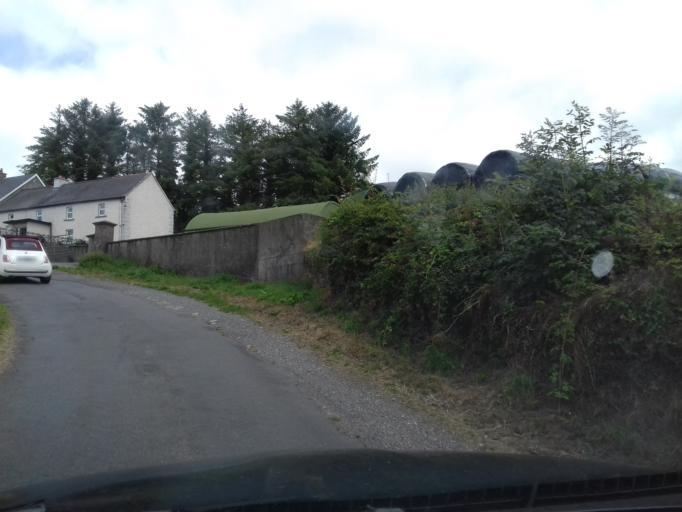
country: IE
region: Leinster
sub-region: Kilkenny
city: Graiguenamanagh
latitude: 52.6199
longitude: -6.8415
